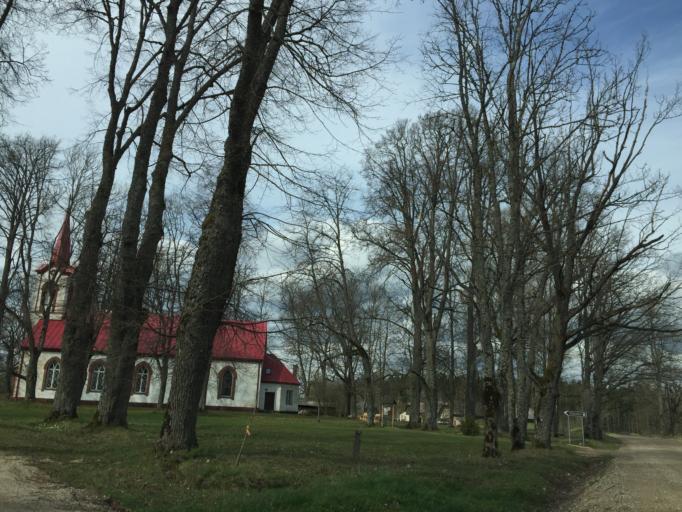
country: LV
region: Ligatne
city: Ligatne
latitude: 57.2167
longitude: 25.0696
